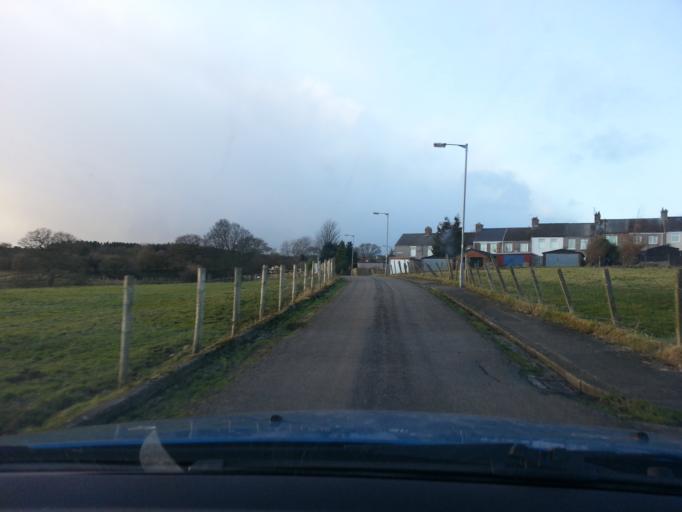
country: GB
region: England
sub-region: County Durham
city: Crook
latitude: 54.7256
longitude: -1.7595
